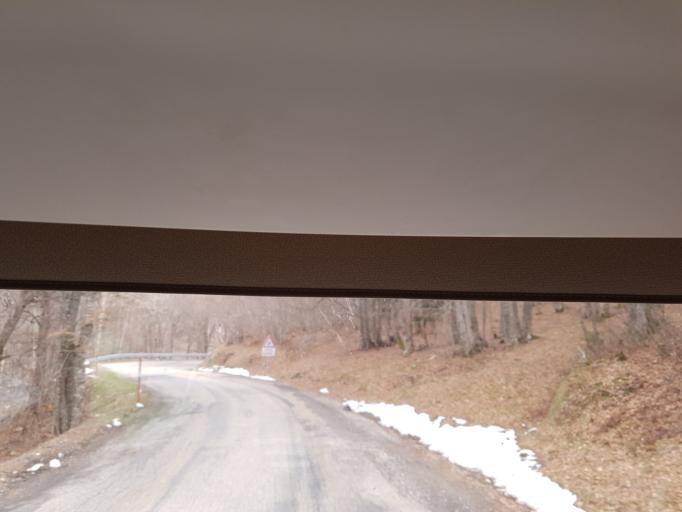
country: FR
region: Languedoc-Roussillon
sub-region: Departement de l'Aude
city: Quillan
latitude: 42.6786
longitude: 2.1325
